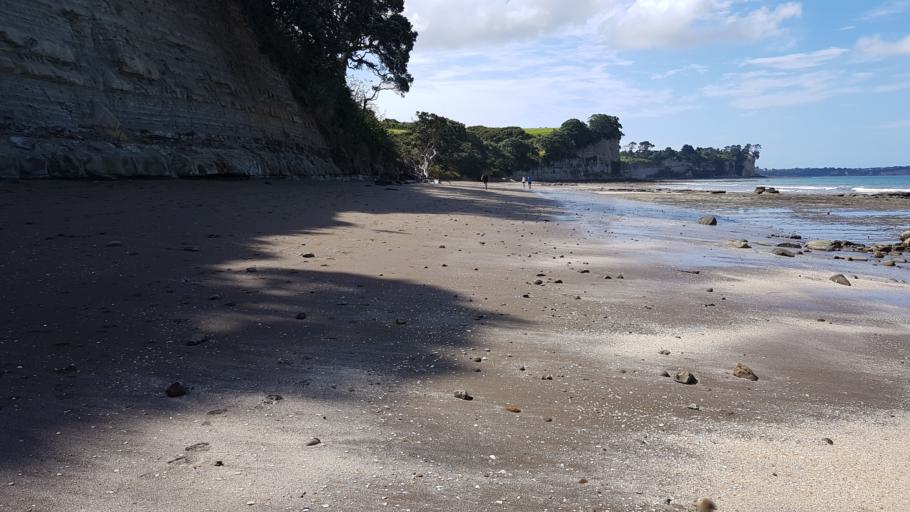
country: NZ
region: Auckland
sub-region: Auckland
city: Rothesay Bay
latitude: -36.6761
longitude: 174.7481
